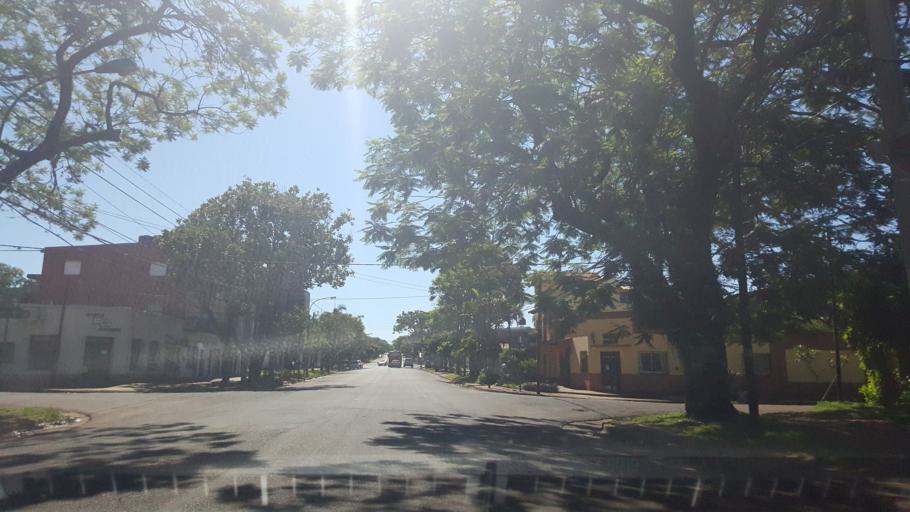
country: AR
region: Misiones
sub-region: Departamento de Capital
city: Posadas
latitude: -27.3841
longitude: -55.9020
